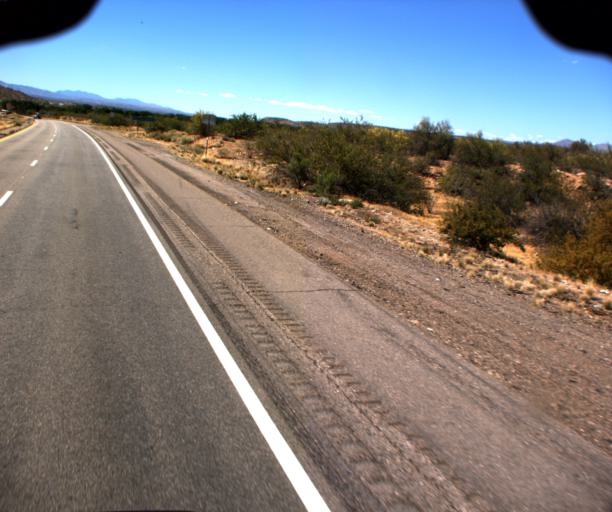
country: US
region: Arizona
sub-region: Yavapai County
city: Bagdad
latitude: 34.6591
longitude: -113.5771
